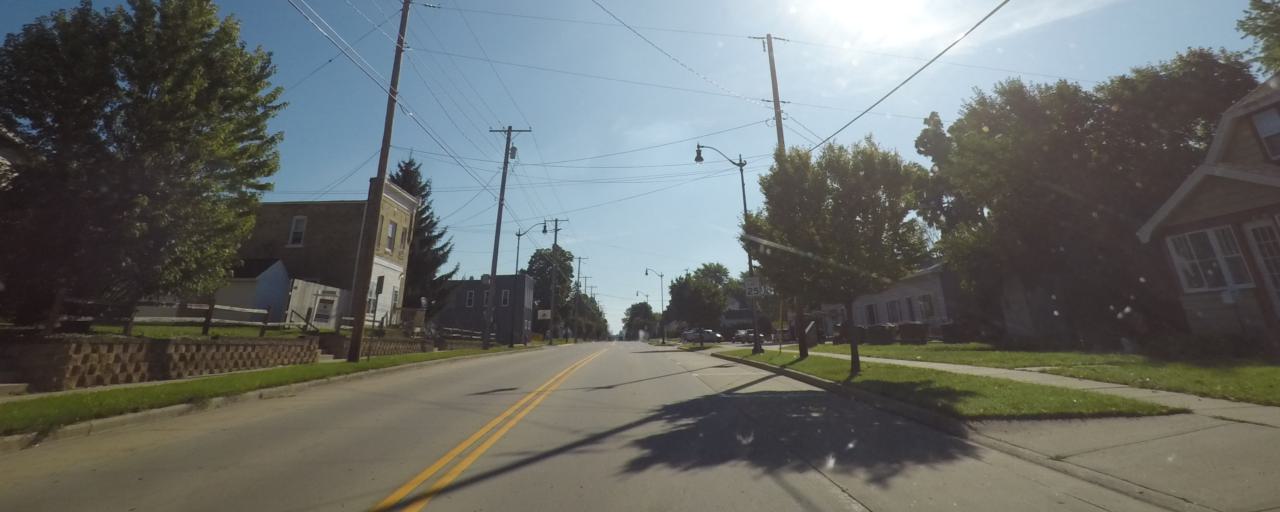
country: US
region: Wisconsin
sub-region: Jefferson County
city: Jefferson
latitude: 43.0051
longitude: -88.7986
